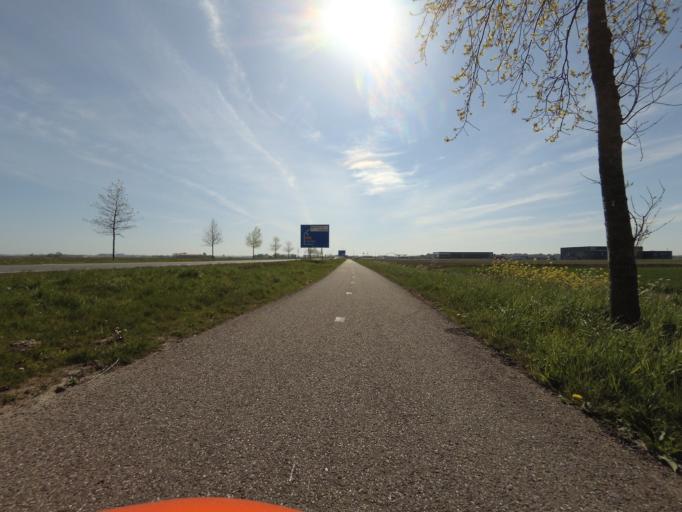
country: NL
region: Flevoland
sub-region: Gemeente Dronten
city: Dronten
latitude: 52.5531
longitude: 5.6899
